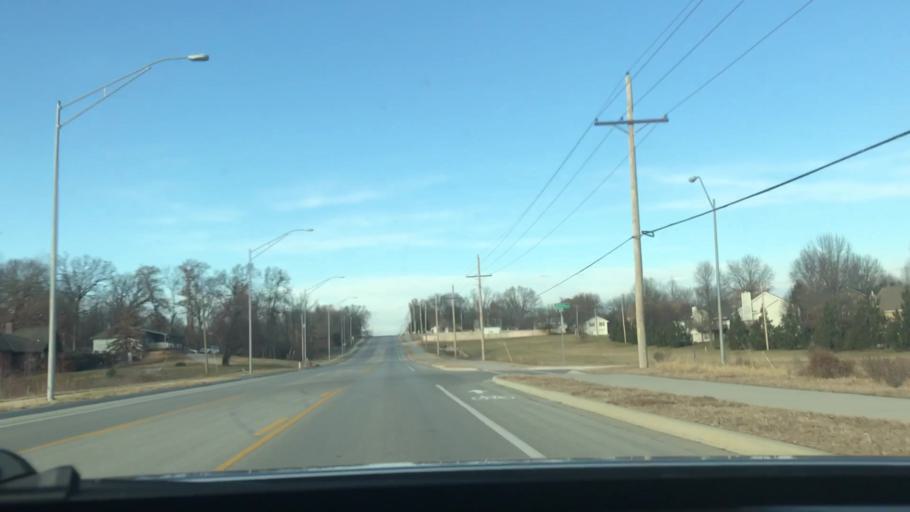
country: US
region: Missouri
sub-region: Jackson County
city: Independence
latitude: 39.0237
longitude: -94.3883
